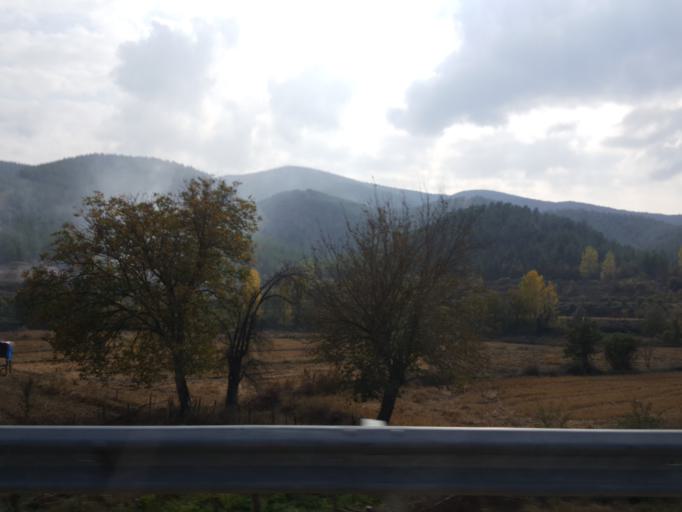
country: TR
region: Sinop
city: Sarayduzu
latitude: 41.3851
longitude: 34.9306
